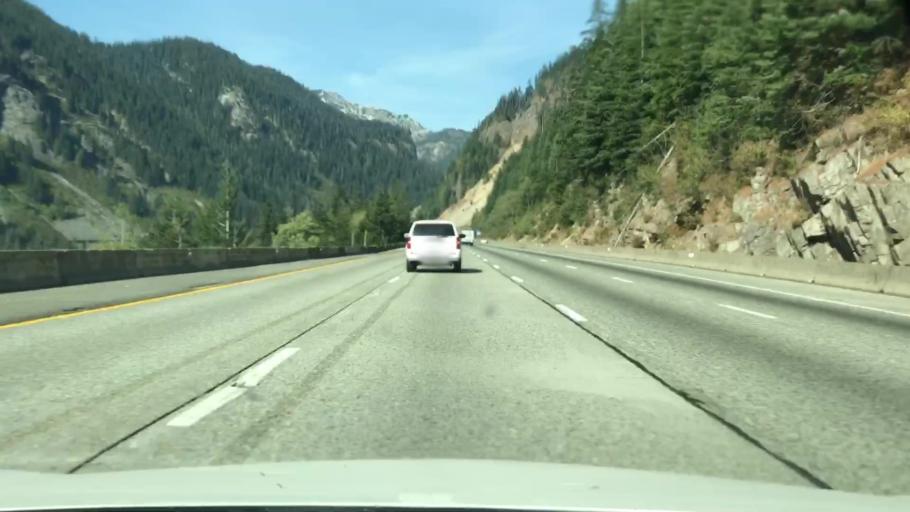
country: US
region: Washington
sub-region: King County
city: Tanner
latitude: 47.4139
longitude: -121.4385
